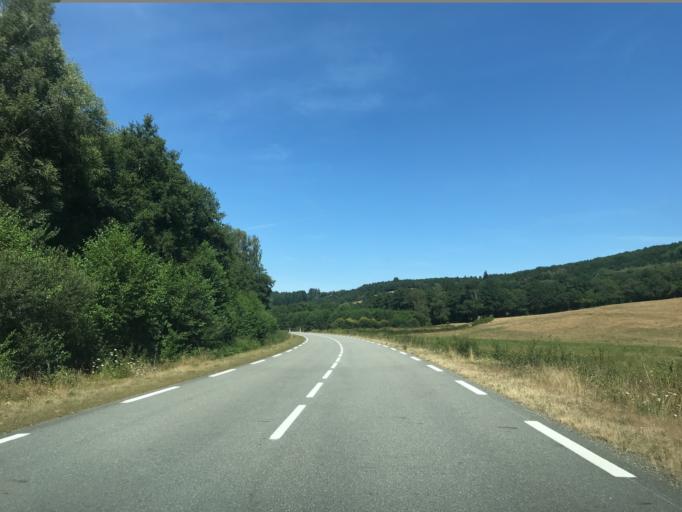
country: FR
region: Limousin
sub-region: Departement de la Creuse
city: Felletin
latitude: 45.8278
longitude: 2.1718
